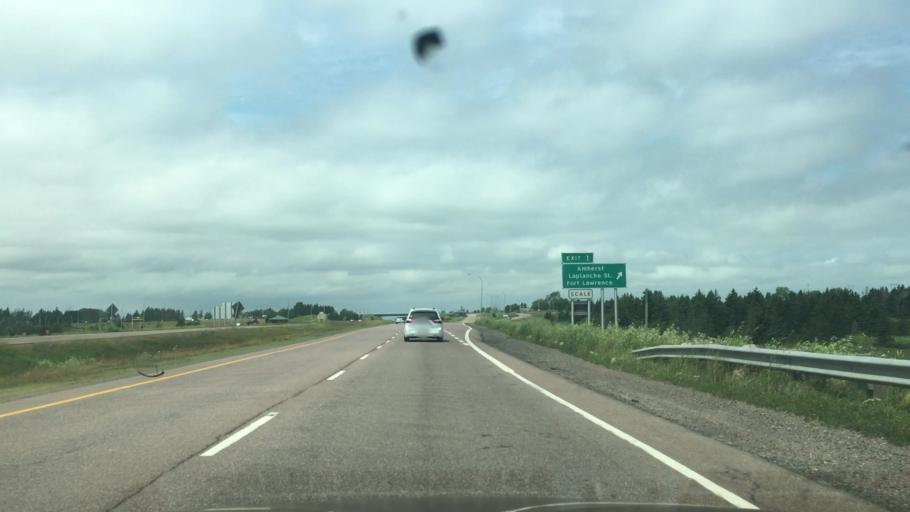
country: CA
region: Nova Scotia
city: Amherst
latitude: 45.8487
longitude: -64.2454
